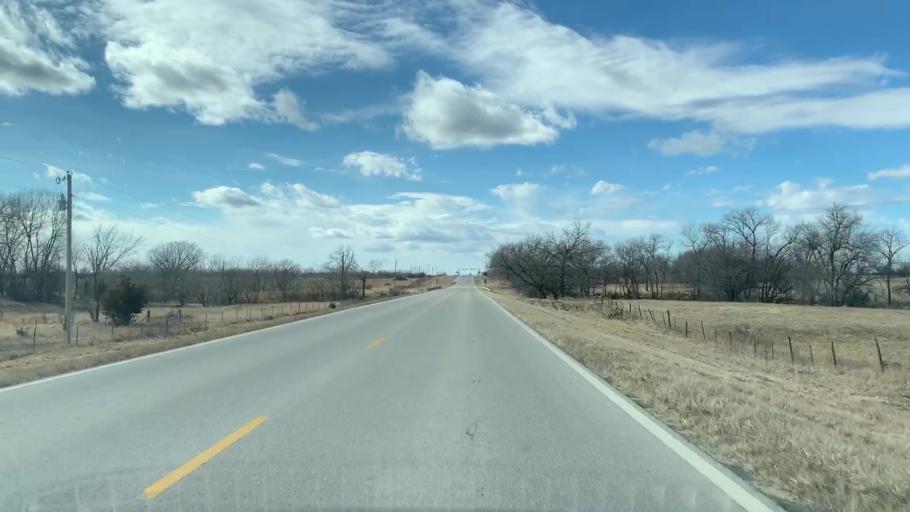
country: US
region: Kansas
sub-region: Neosho County
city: Chanute
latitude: 37.5288
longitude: -95.4617
